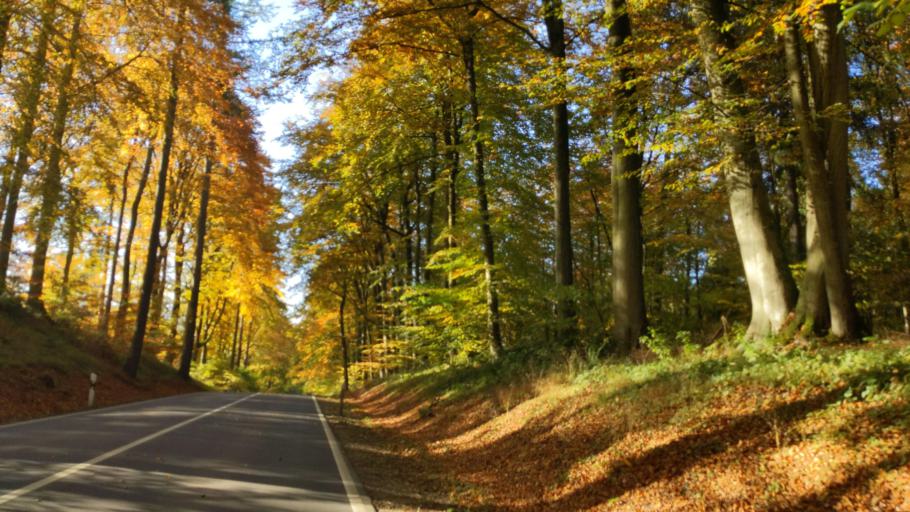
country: DE
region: Schleswig-Holstein
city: Kasseedorf
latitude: 54.1482
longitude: 10.6933
